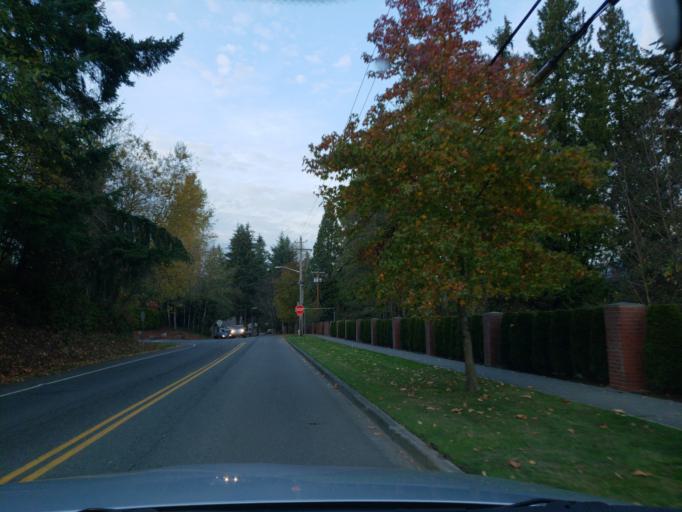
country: US
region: Washington
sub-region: King County
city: Bothell
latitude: 47.7463
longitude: -122.1914
